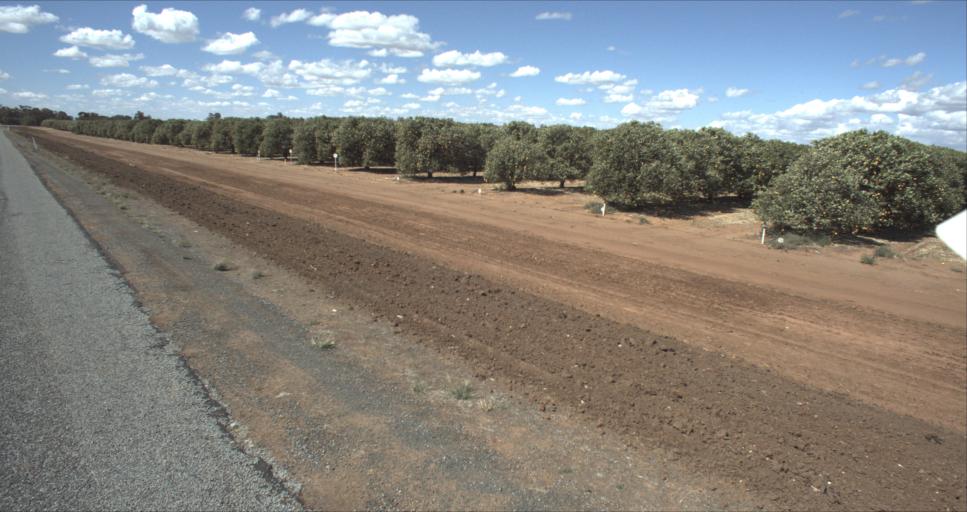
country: AU
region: New South Wales
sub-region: Leeton
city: Leeton
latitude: -34.5214
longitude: 146.2237
